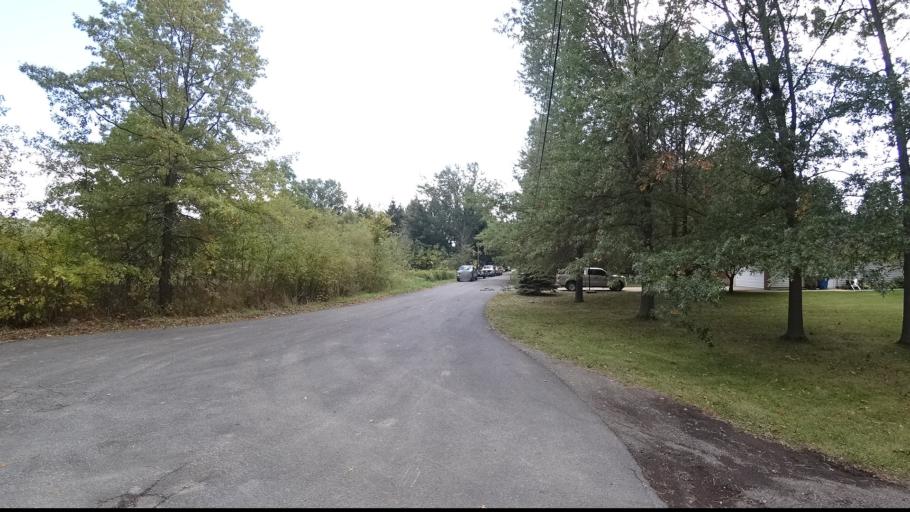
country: US
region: Indiana
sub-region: Porter County
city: Burns Harbor
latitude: 41.6147
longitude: -87.1158
